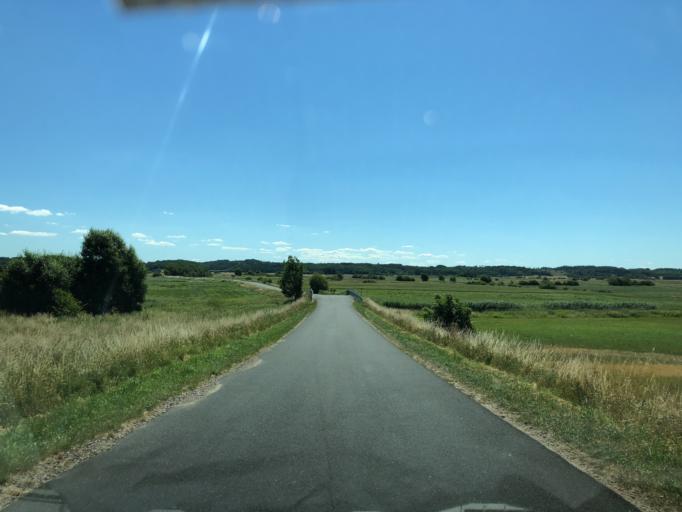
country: DK
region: Central Jutland
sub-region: Viborg Kommune
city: Viborg
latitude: 56.5534
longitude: 9.4264
